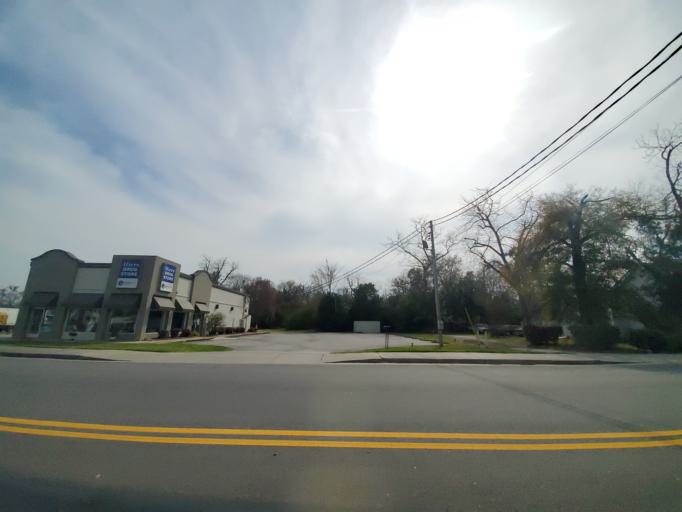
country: US
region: South Carolina
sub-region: Bamberg County
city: Bamberg
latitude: 33.2980
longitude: -81.0386
